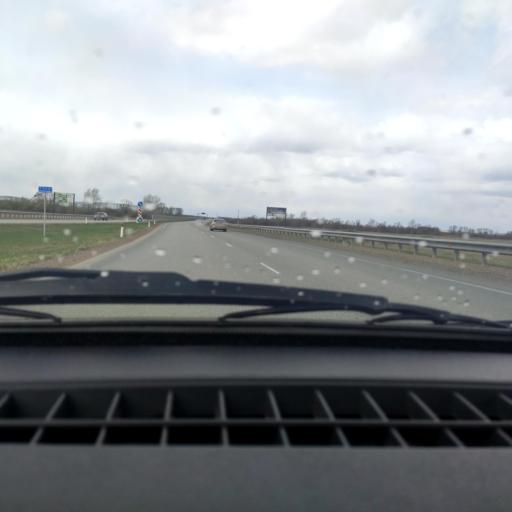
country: RU
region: Bashkortostan
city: Asanovo
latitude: 54.9674
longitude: 55.5815
